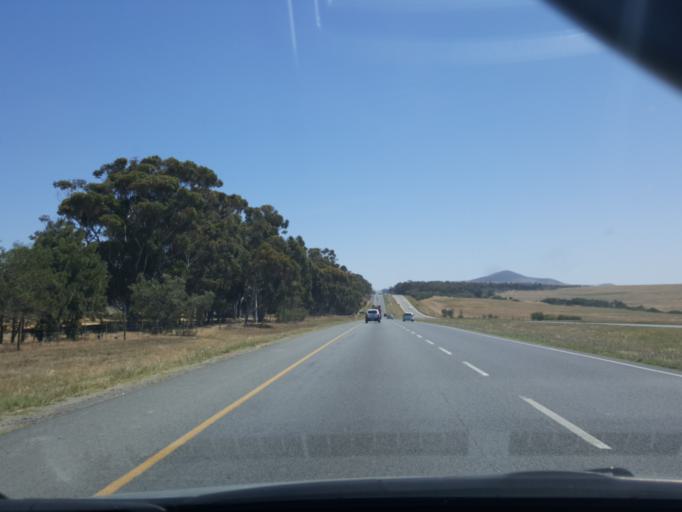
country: ZA
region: Western Cape
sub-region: City of Cape Town
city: Sunset Beach
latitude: -33.7829
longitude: 18.5489
